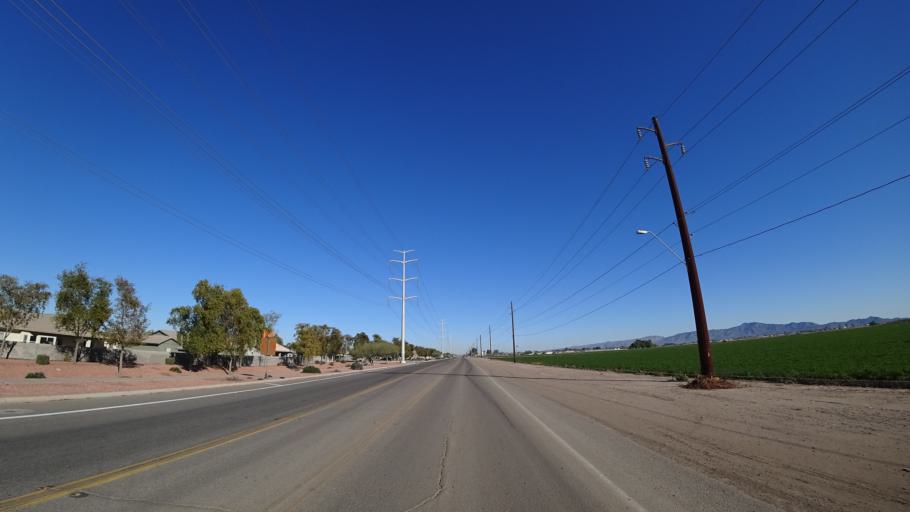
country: US
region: Arizona
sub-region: Maricopa County
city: Tolleson
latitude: 33.4084
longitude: -112.2287
